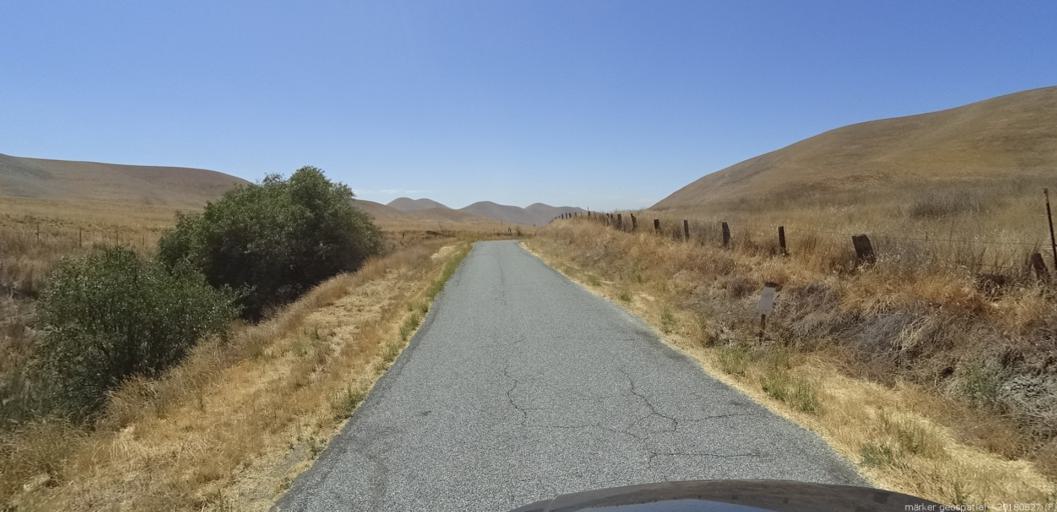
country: US
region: California
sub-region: Monterey County
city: King City
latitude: 36.1162
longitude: -120.8732
